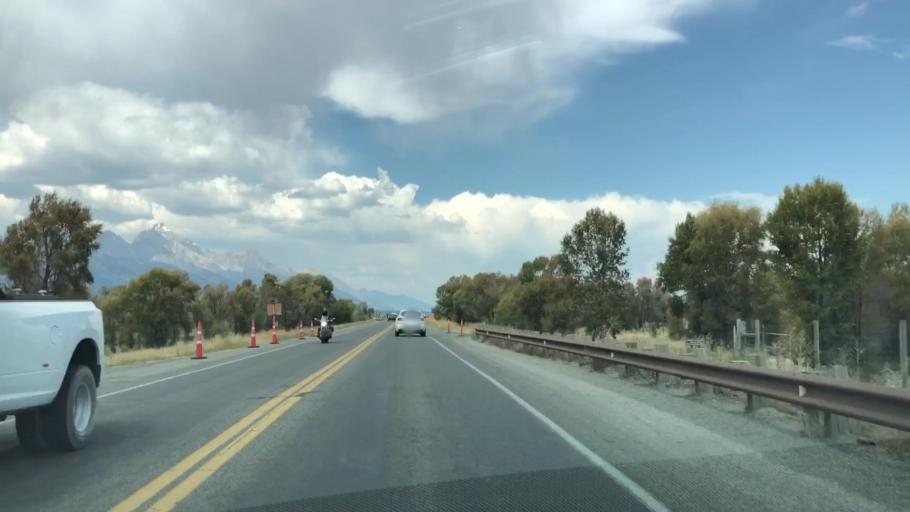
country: US
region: Wyoming
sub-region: Teton County
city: Jackson
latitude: 43.5672
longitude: -110.7331
